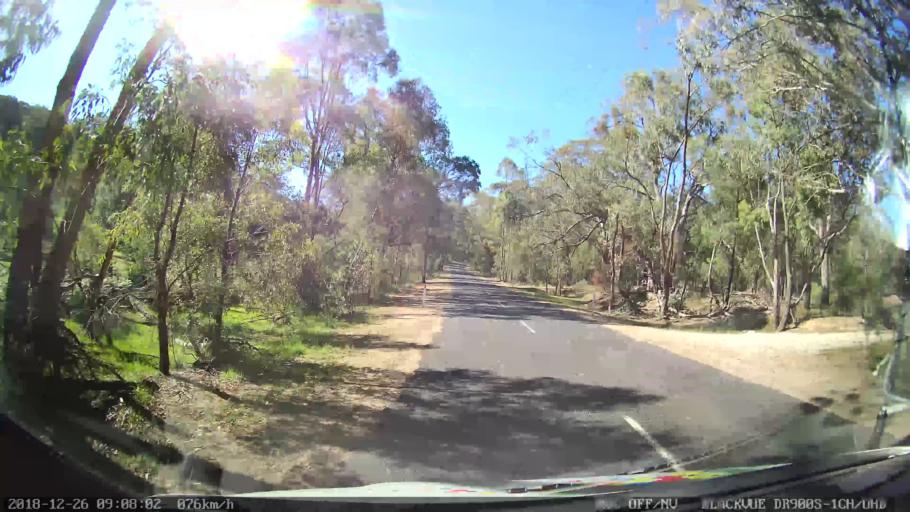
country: AU
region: New South Wales
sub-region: Mid-Western Regional
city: Kandos
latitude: -32.7121
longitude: 150.0030
